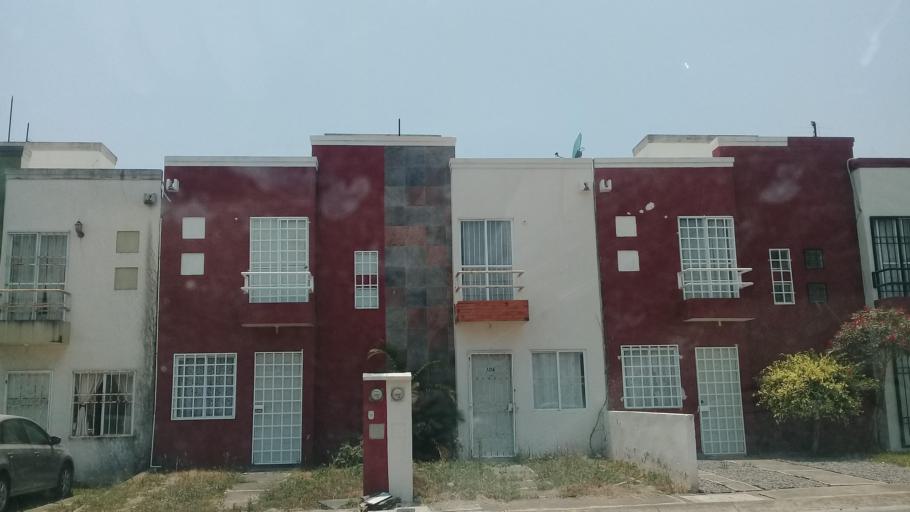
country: MX
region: Veracruz
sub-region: Veracruz
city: Hacienda Sotavento
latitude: 19.1326
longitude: -96.1755
